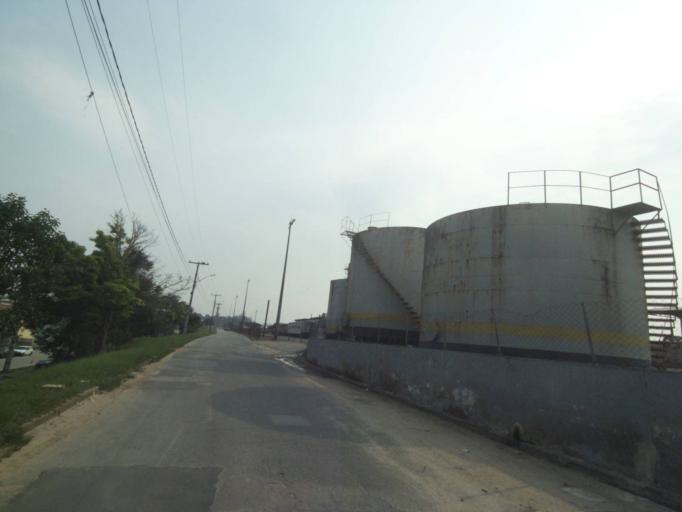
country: BR
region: Parana
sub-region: Sao Jose Dos Pinhais
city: Sao Jose dos Pinhais
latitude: -25.5337
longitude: -49.2314
